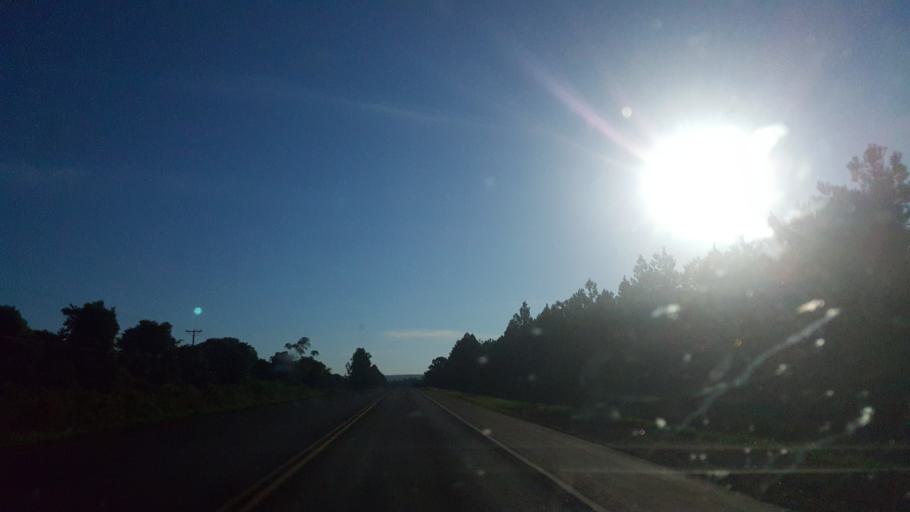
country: AR
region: Misiones
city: El Alcazar
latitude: -26.6694
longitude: -54.7702
